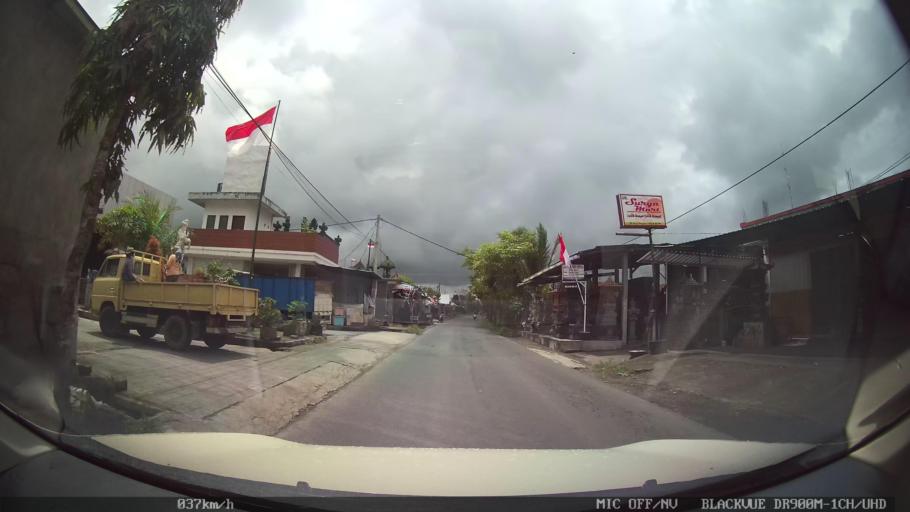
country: ID
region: Bali
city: Banjar Pekenjelodan
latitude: -8.5637
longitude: 115.1860
